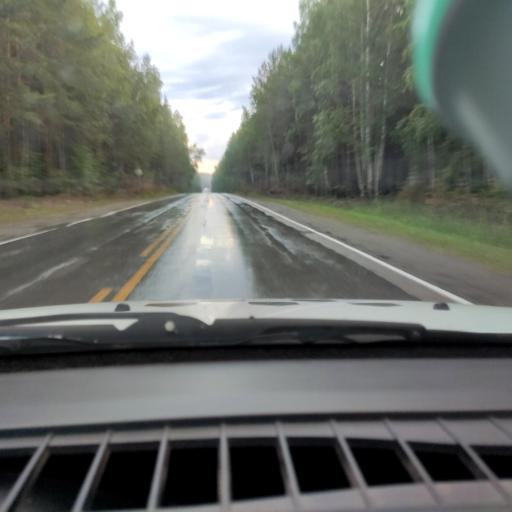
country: RU
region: Chelyabinsk
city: Kyshtym
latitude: 55.7494
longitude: 60.5508
